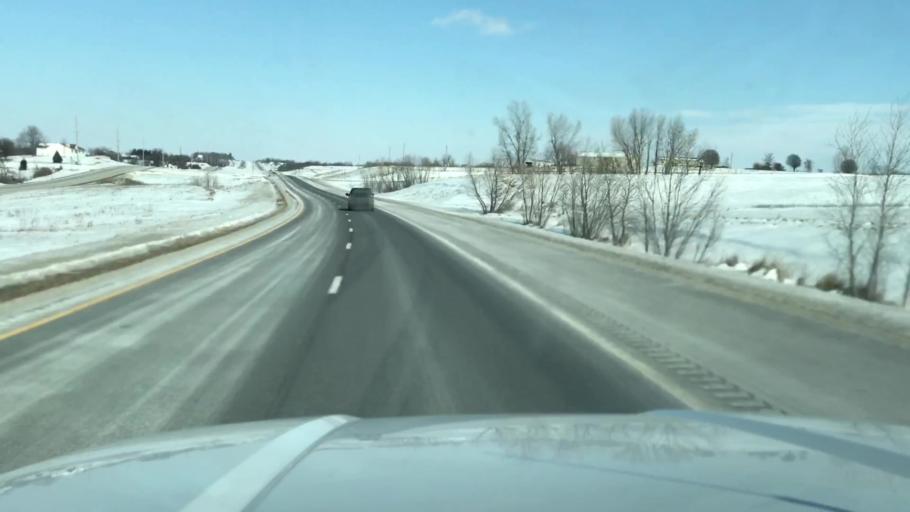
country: US
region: Missouri
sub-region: Nodaway County
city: Maryville
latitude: 40.1832
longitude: -94.8680
